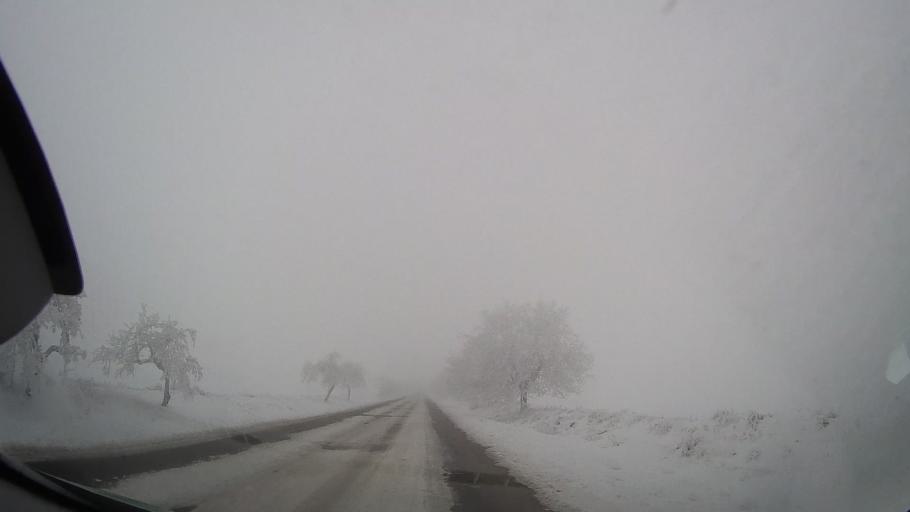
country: RO
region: Neamt
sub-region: Comuna Valea Ursului
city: Valea Ursului
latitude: 46.8185
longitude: 27.0648
